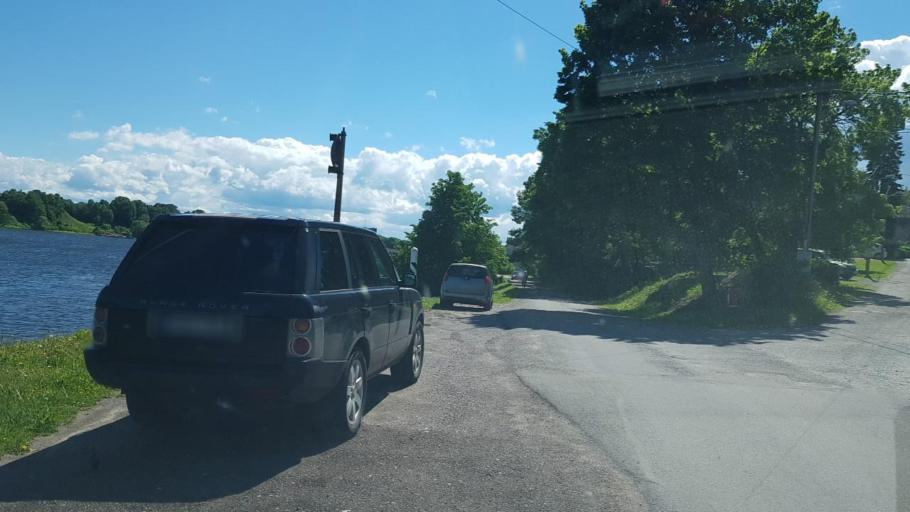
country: EE
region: Ida-Virumaa
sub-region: Narva linn
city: Narva
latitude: 59.3865
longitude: 28.2029
